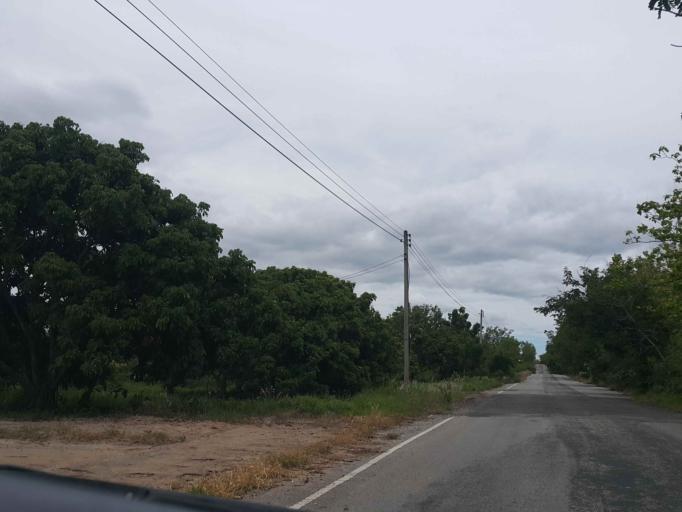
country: TH
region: Chiang Mai
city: Doi Lo
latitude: 18.5059
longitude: 98.7635
